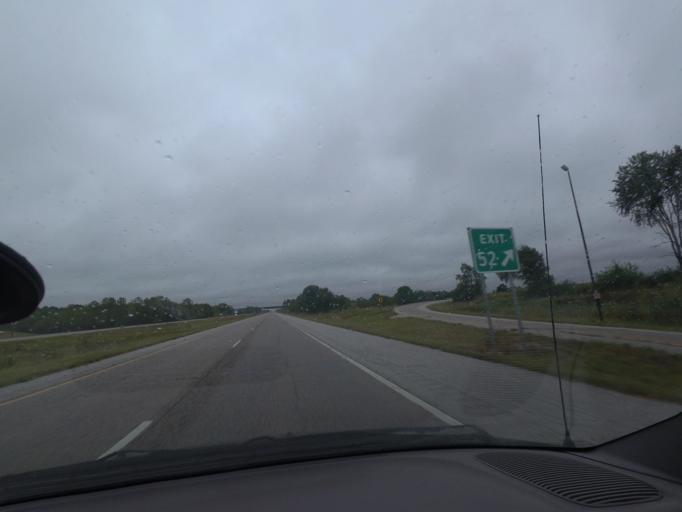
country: US
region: Illinois
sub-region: Scott County
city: Winchester
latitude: 39.6810
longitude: -90.4612
